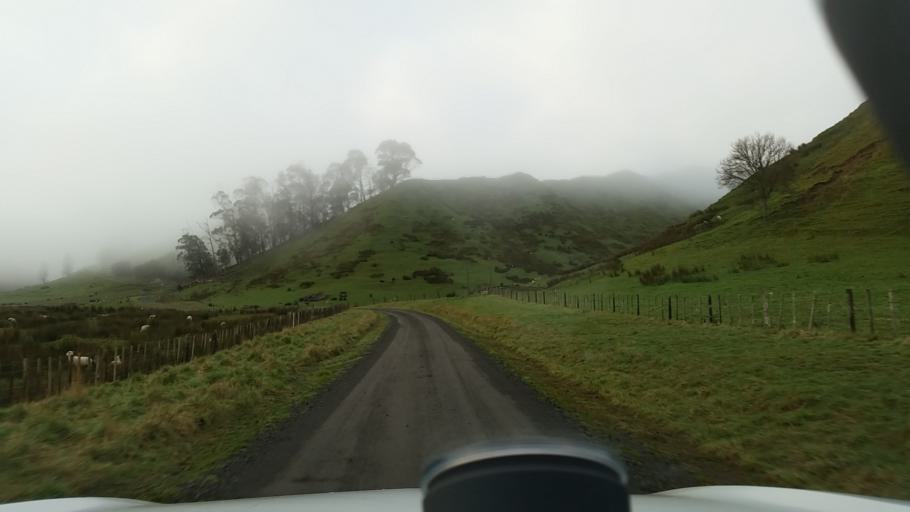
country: NZ
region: Taranaki
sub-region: South Taranaki District
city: Eltham
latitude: -39.4309
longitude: 174.4414
